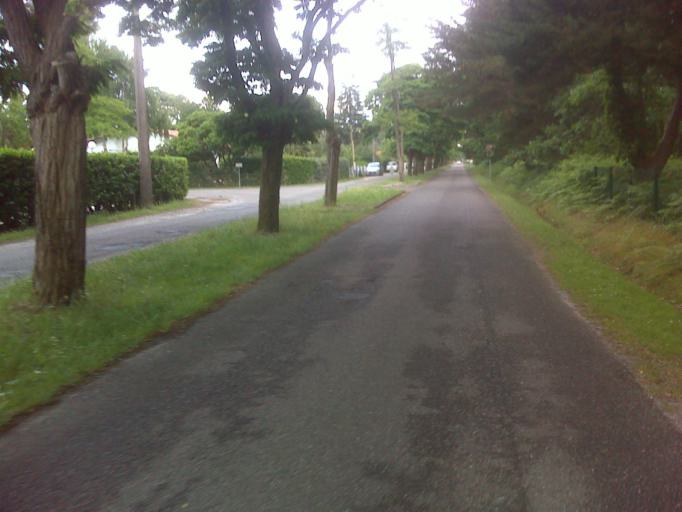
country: FR
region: Aquitaine
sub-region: Departement de la Gironde
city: Ares
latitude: 44.7562
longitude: -1.1321
